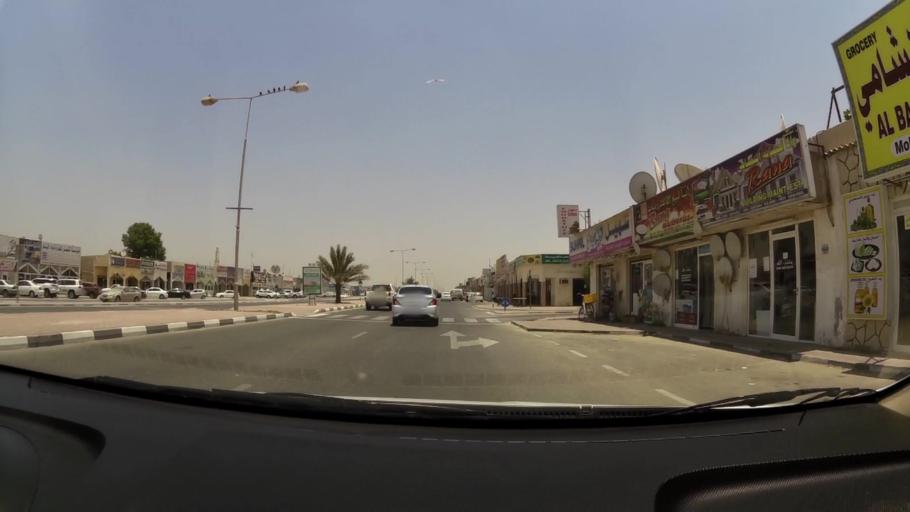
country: AE
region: Umm al Qaywayn
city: Umm al Qaywayn
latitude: 25.5523
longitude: 55.5496
